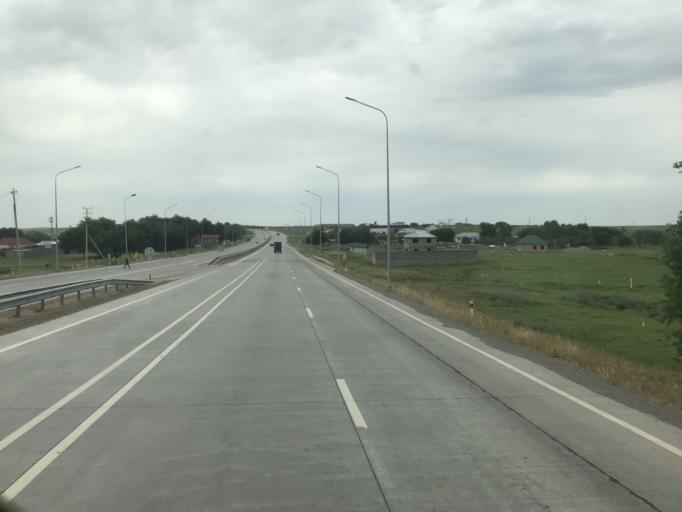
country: KZ
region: Ongtustik Qazaqstan
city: Shymkent
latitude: 42.2129
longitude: 69.5212
